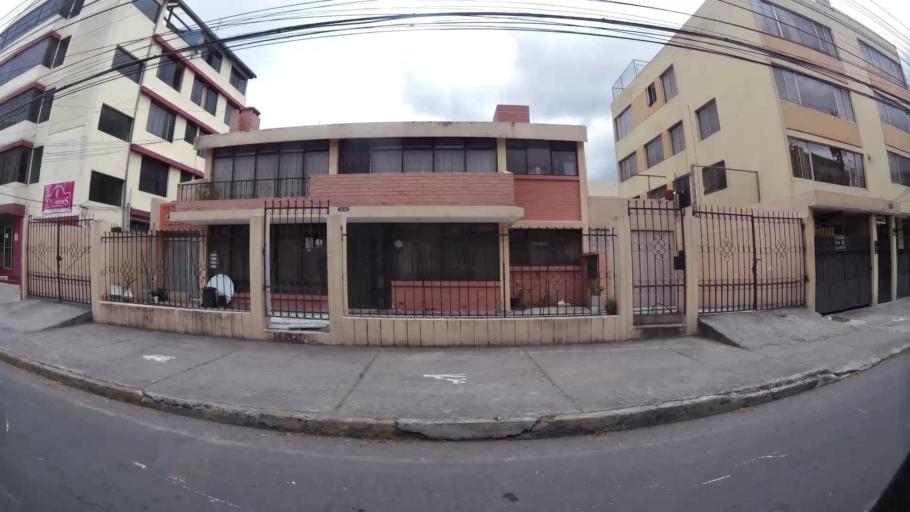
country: EC
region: Pichincha
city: Quito
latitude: -0.1705
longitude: -78.4789
